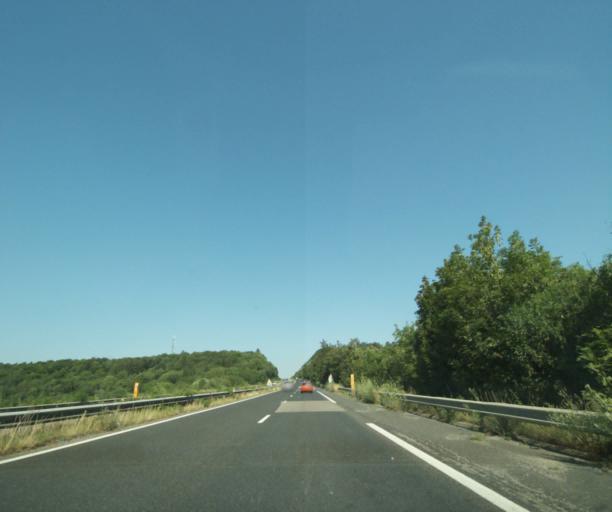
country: FR
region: Lorraine
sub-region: Departement de Meurthe-et-Moselle
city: Foug
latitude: 48.6719
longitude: 5.7778
